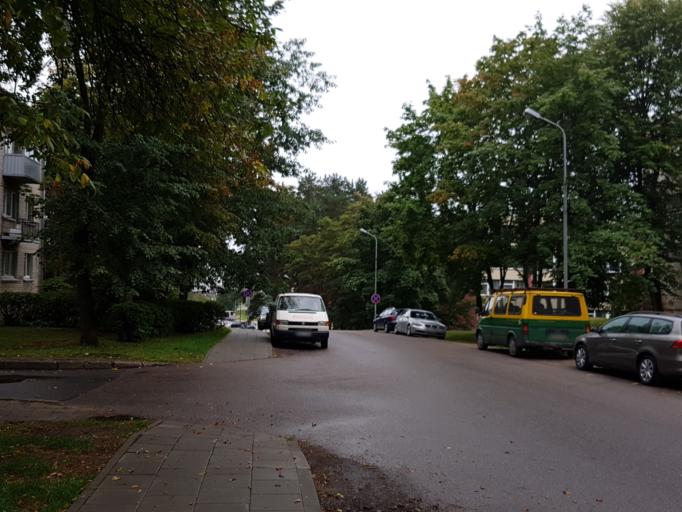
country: LT
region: Vilnius County
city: Lazdynai
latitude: 54.6697
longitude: 25.2154
